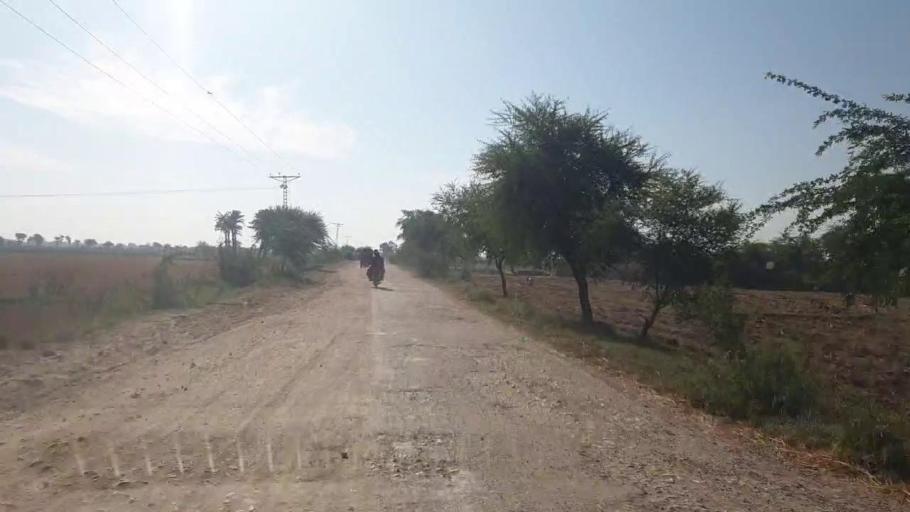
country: PK
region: Sindh
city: Talhar
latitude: 24.9070
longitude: 68.8209
